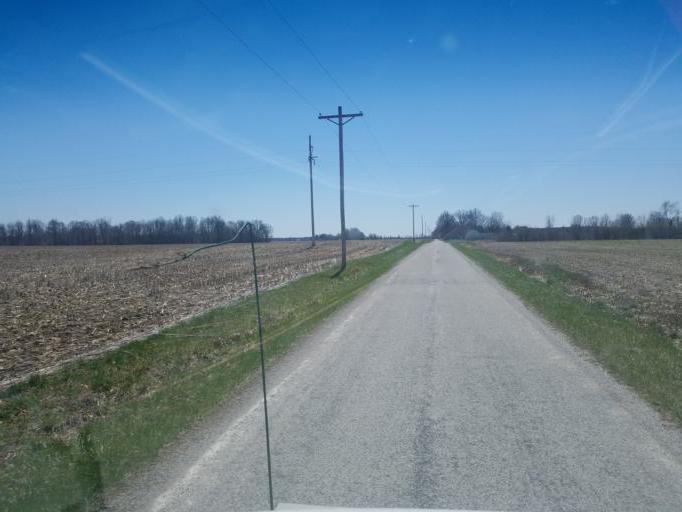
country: US
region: Ohio
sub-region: Morrow County
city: Cardington
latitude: 40.5661
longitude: -82.9527
